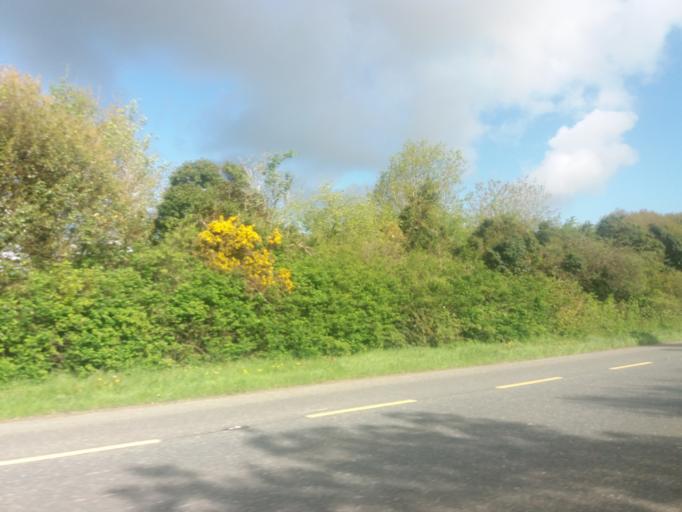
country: IE
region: Leinster
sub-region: Loch Garman
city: Enniscorthy
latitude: 52.5356
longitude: -6.5537
